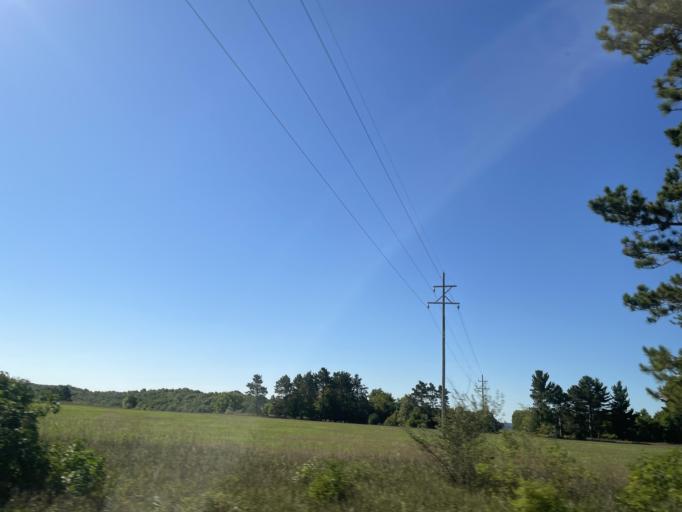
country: US
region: Michigan
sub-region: Benzie County
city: Beulah
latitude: 44.6173
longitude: -86.0696
